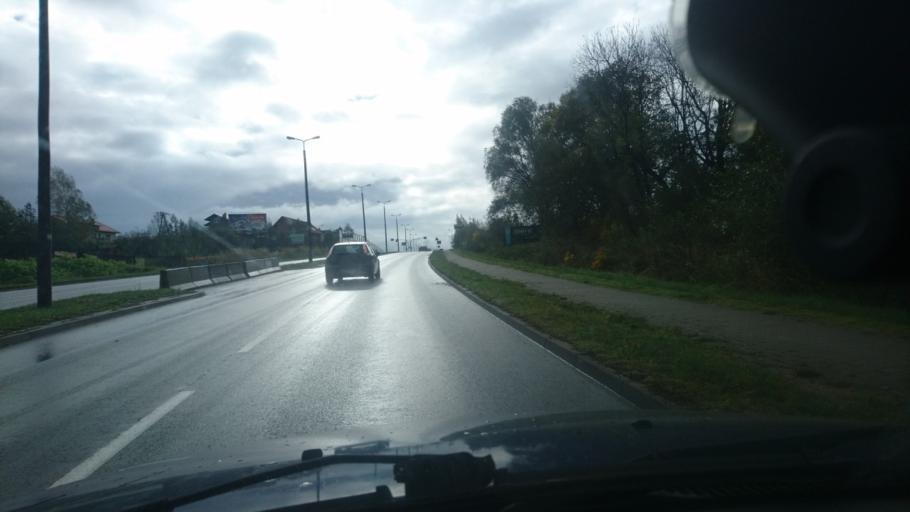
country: PL
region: Silesian Voivodeship
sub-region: Bielsko-Biala
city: Bielsko-Biala
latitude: 49.8310
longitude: 19.0116
